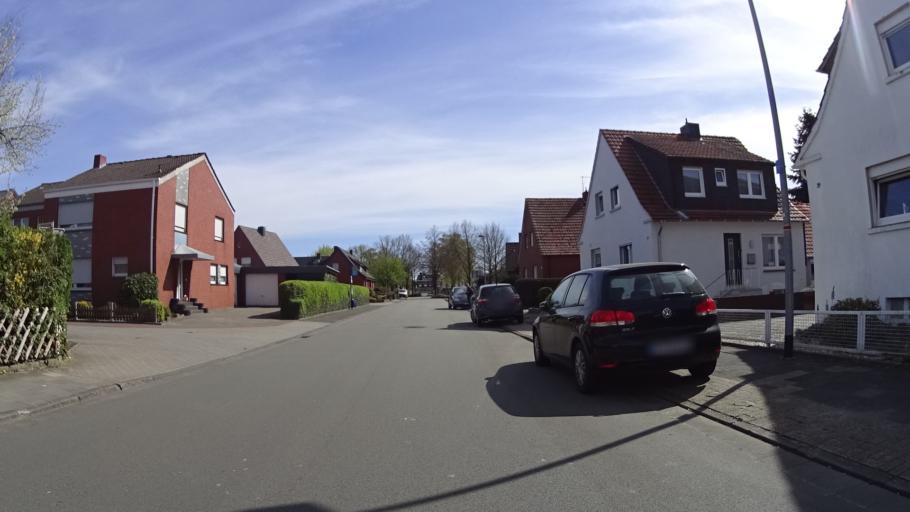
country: DE
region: North Rhine-Westphalia
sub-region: Regierungsbezirk Munster
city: Dreierwalde
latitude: 52.2889
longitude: 7.4732
